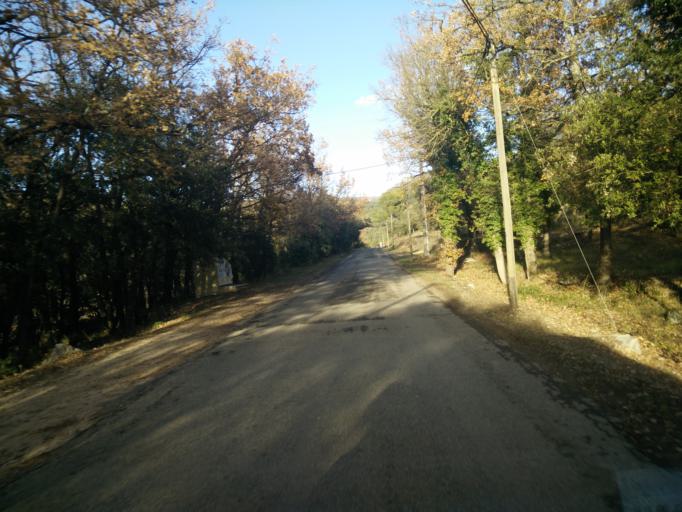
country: FR
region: Provence-Alpes-Cote d'Azur
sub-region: Departement du Var
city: Signes
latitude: 43.2828
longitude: 5.8438
